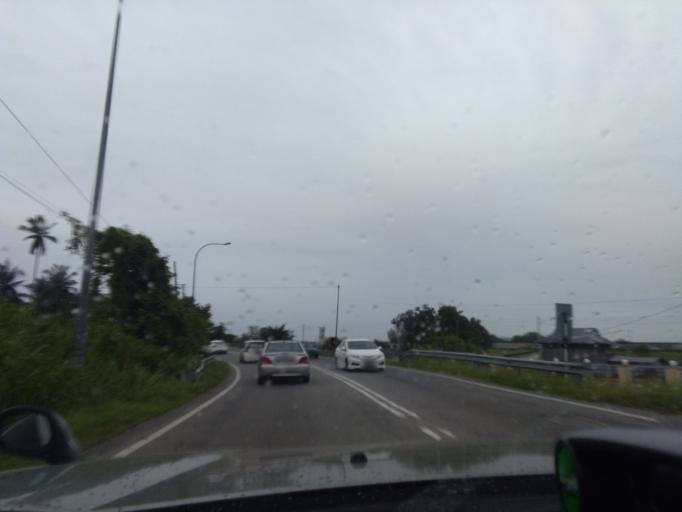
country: MY
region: Penang
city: Nibong Tebal
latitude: 5.1620
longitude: 100.4786
